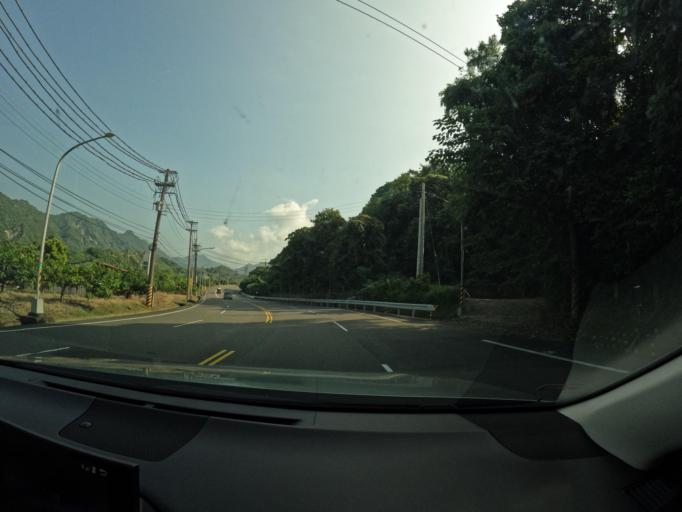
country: TW
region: Taiwan
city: Yujing
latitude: 23.0817
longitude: 120.5215
